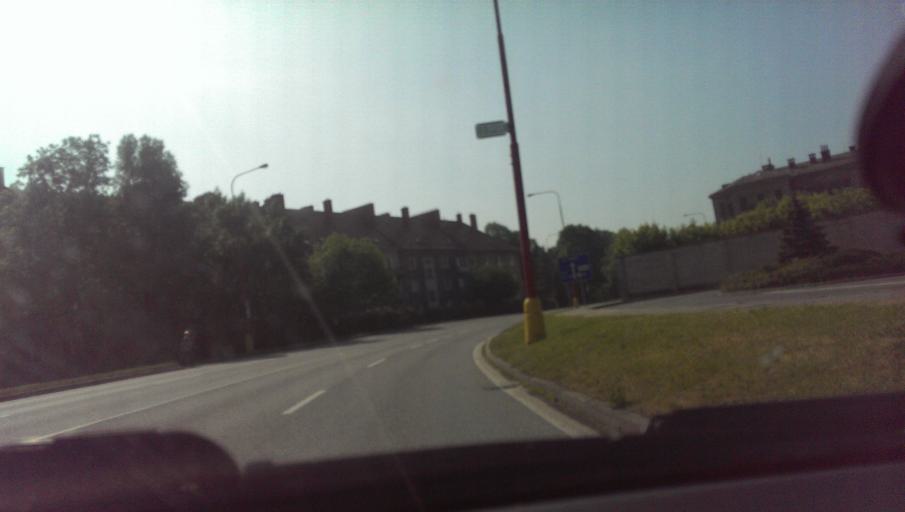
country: CZ
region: Zlin
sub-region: Okres Uherske Hradiste
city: Uherske Hradiste
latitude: 49.0702
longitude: 17.4662
